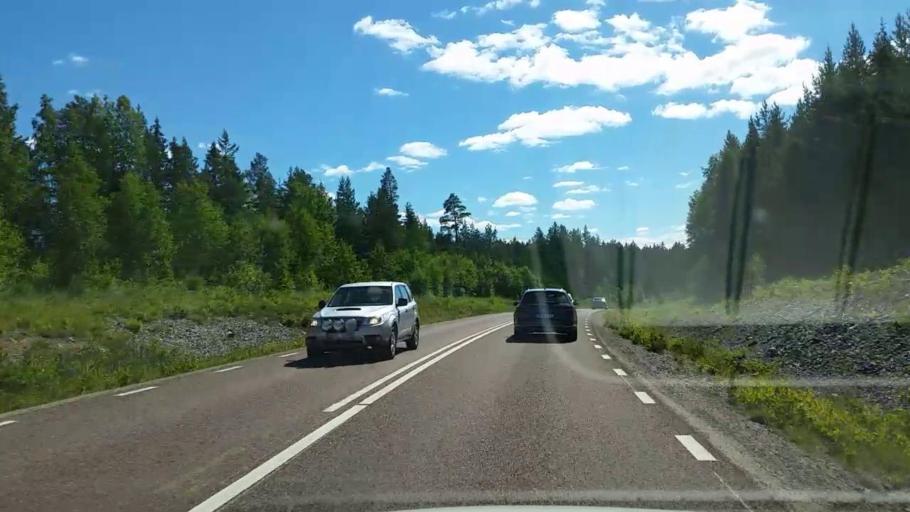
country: SE
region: Gaevleborg
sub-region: Ovanakers Kommun
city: Edsbyn
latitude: 61.2175
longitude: 15.8772
